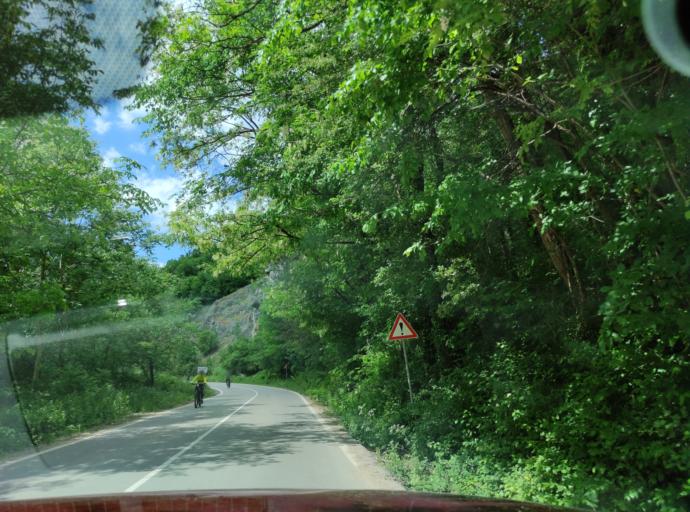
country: BG
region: Montana
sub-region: Obshtina Chiprovtsi
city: Chiprovtsi
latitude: 43.4414
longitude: 22.9349
